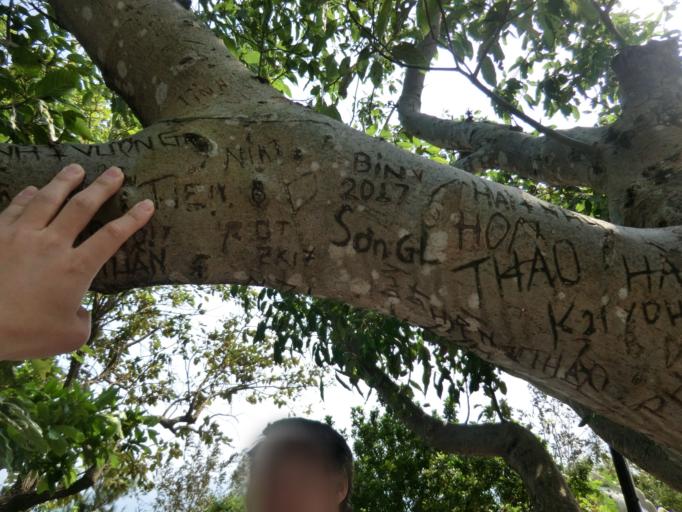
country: VN
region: Da Nang
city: Son Tra
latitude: 16.0991
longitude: 108.2768
